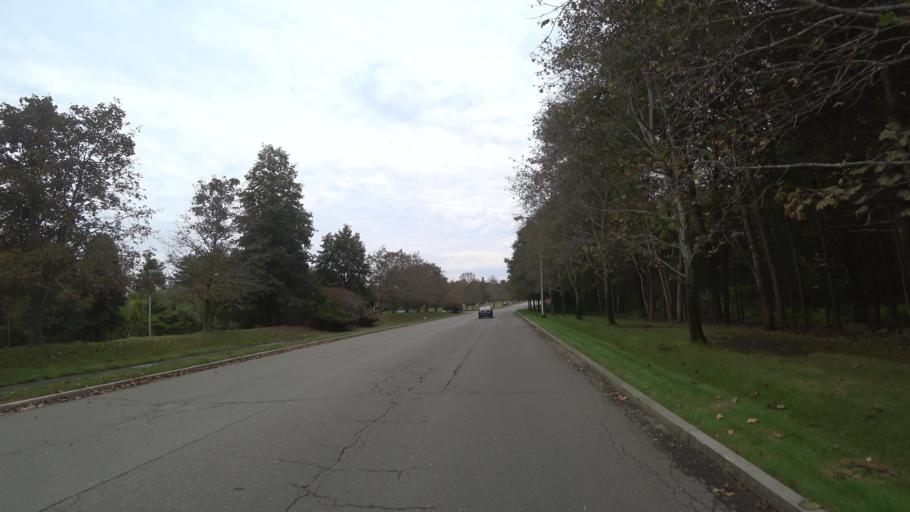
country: US
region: Massachusetts
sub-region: Middlesex County
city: Wilmington
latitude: 42.6021
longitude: -71.1609
